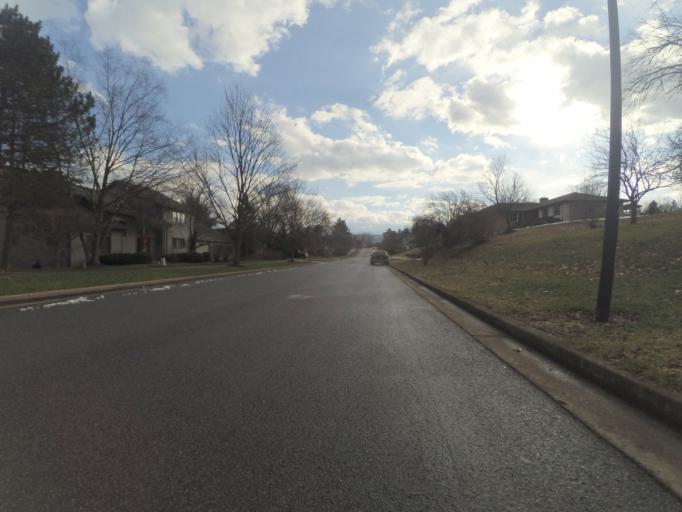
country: US
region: Pennsylvania
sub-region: Centre County
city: State College
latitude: 40.7927
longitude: -77.8363
